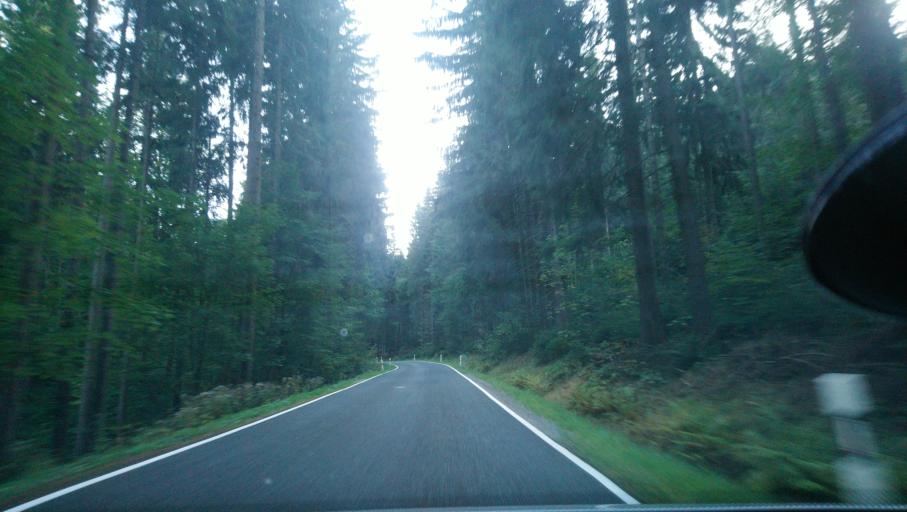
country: DE
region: Saxony
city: Barenstein
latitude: 50.5204
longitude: 13.0457
